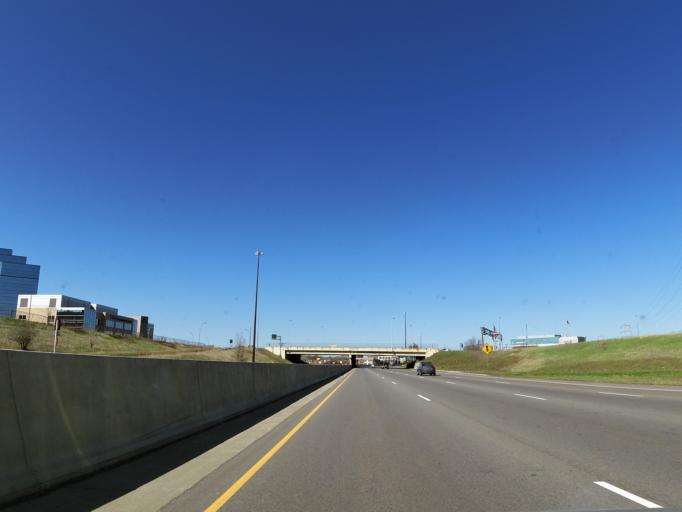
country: US
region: Minnesota
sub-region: Hennepin County
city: Bloomington
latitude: 44.8598
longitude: -93.3261
